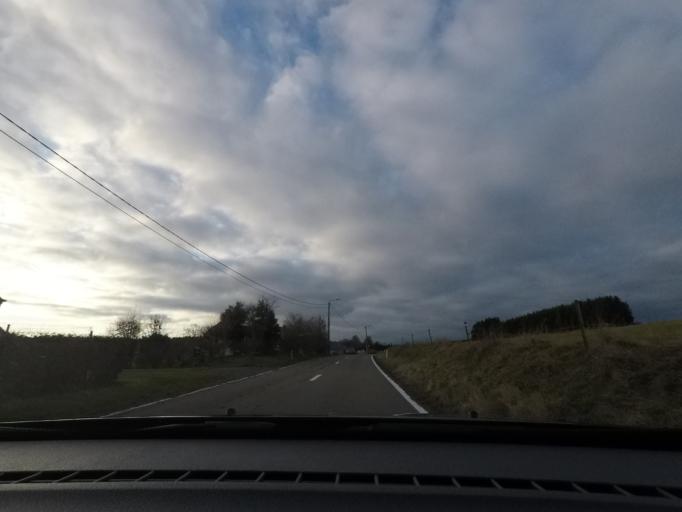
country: BE
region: Wallonia
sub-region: Province du Luxembourg
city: Leglise
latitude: 49.7647
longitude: 5.5099
